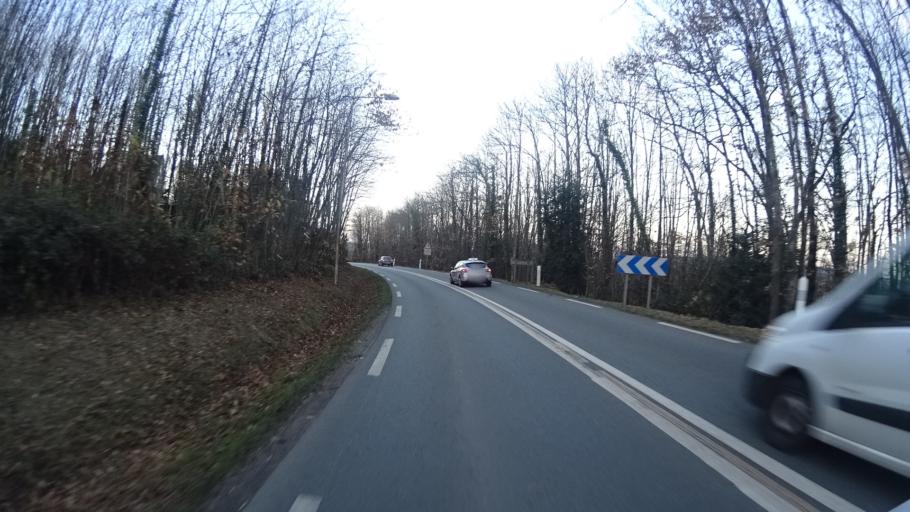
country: FR
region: Pays de la Loire
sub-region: Departement de la Loire-Atlantique
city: Saint-Nicolas-de-Redon
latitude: 47.6454
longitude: -2.0519
